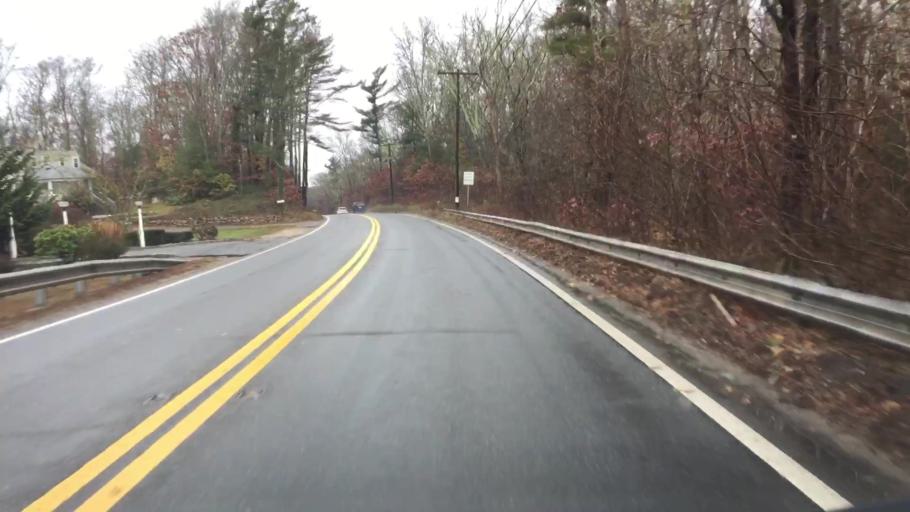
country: US
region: Massachusetts
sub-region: Barnstable County
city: Falmouth
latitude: 41.5711
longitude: -70.6187
